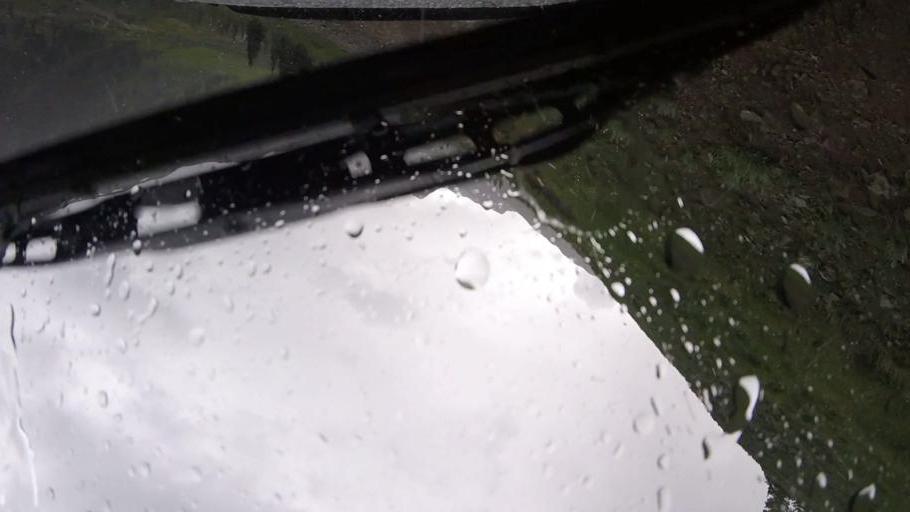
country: US
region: Colorado
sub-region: Ouray County
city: Ouray
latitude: 37.9347
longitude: -107.5693
